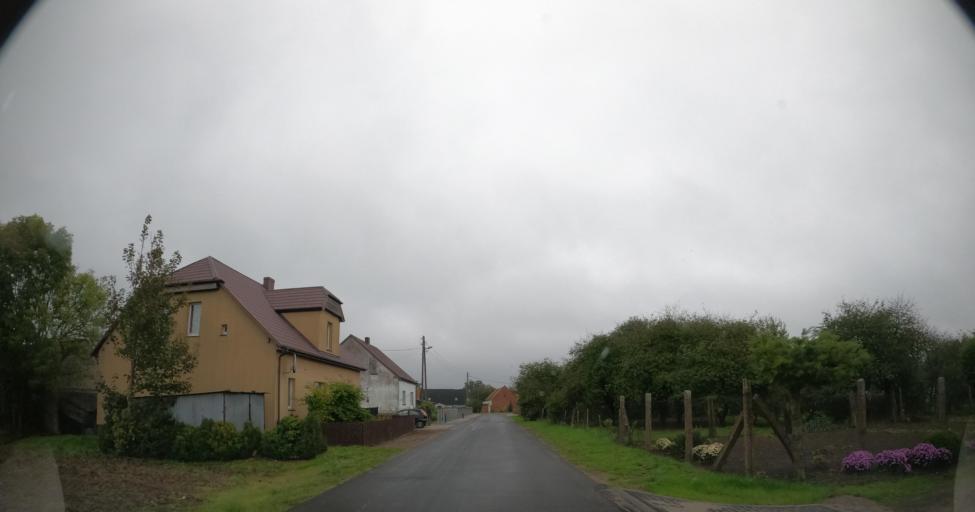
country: PL
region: West Pomeranian Voivodeship
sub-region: Powiat pyrzycki
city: Kozielice
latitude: 53.0749
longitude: 14.7868
